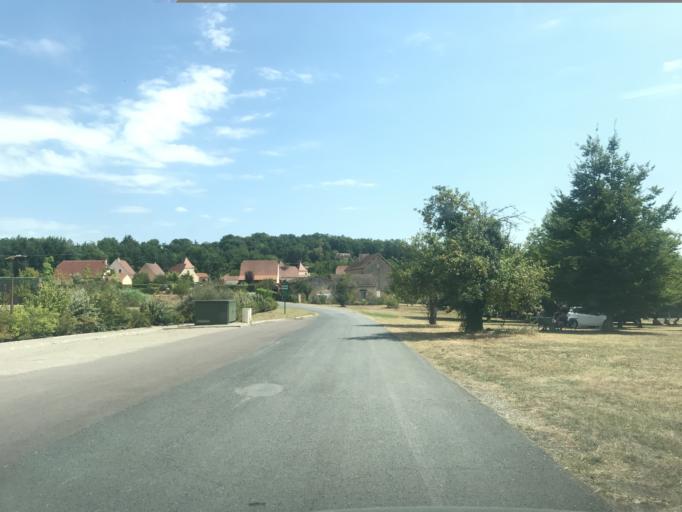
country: FR
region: Aquitaine
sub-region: Departement de la Dordogne
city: Carsac-Aillac
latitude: 44.8277
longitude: 1.2746
